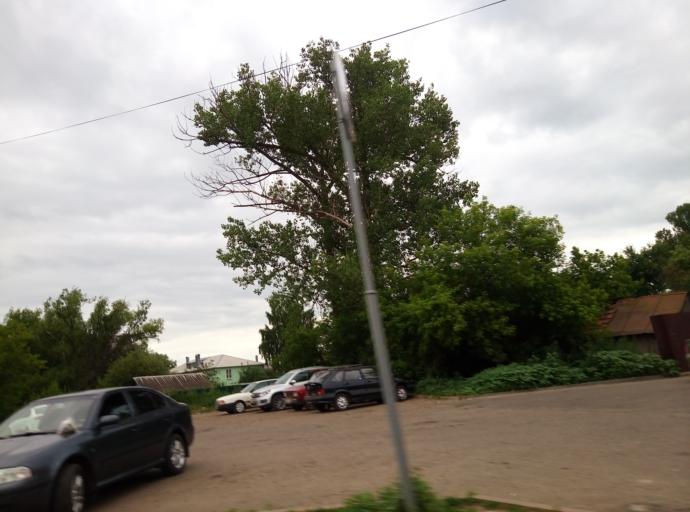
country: RU
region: Kursk
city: Kursk
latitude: 51.7133
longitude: 36.1436
